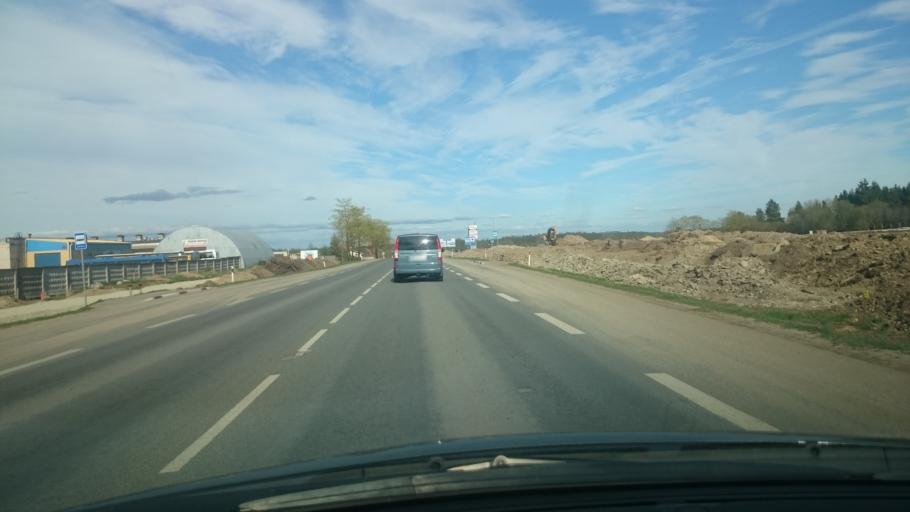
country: EE
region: Ida-Virumaa
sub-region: Sillamaee linn
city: Sillamae
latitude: 59.3913
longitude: 27.7429
